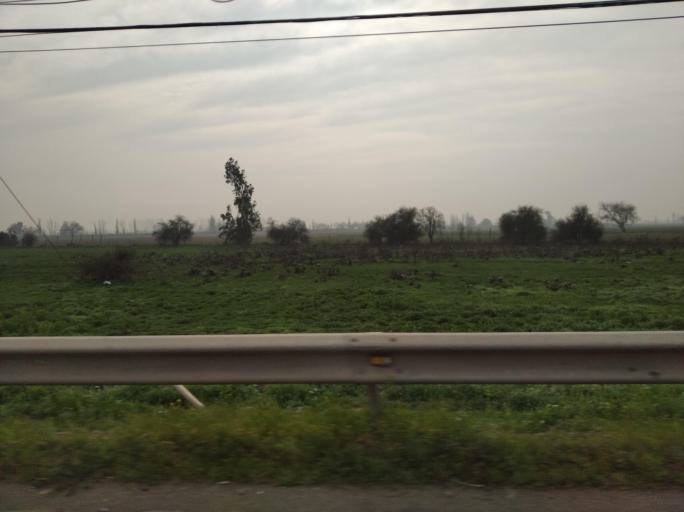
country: CL
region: Santiago Metropolitan
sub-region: Provincia de Chacabuco
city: Lampa
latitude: -33.3372
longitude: -70.8162
